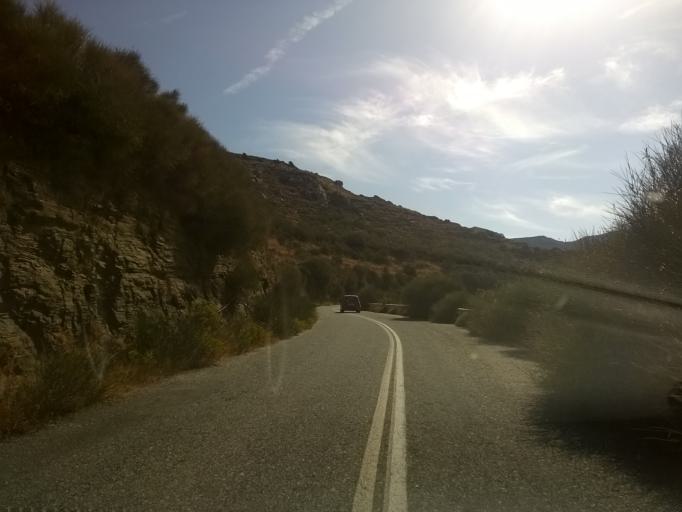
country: GR
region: South Aegean
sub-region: Nomos Kykladon
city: Filotion
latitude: 37.1577
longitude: 25.5537
